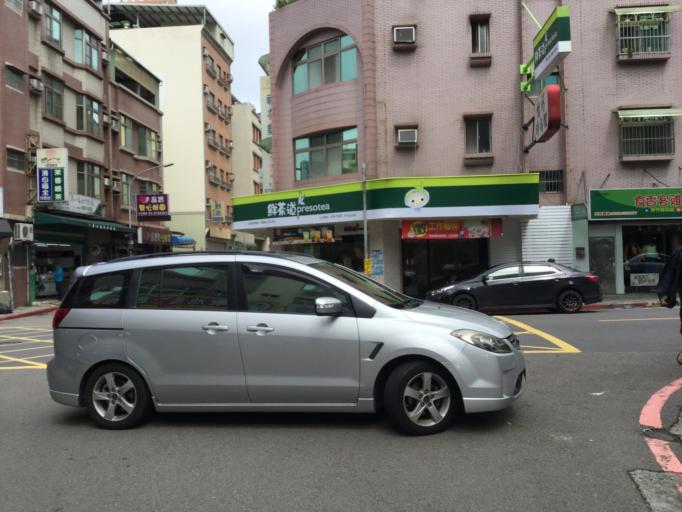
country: TW
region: Taiwan
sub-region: Hsinchu
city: Hsinchu
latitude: 24.7776
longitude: 121.0210
